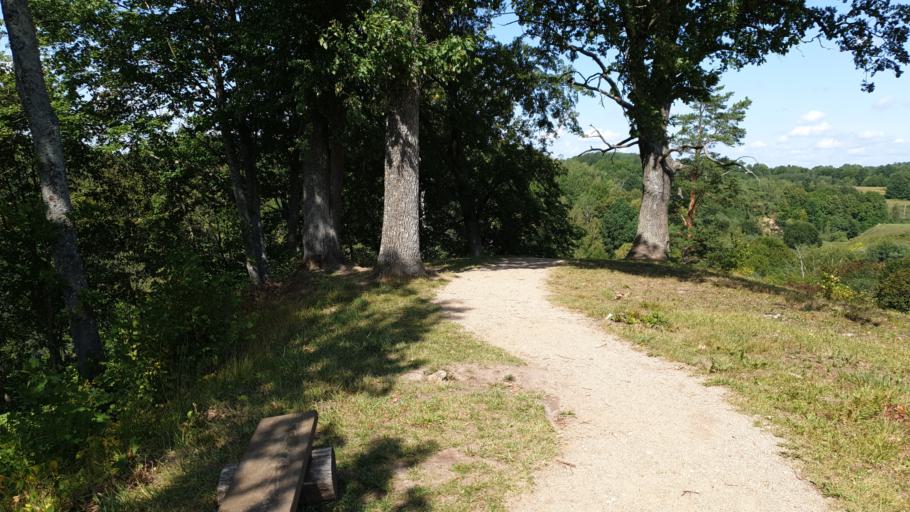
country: LT
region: Vilnius County
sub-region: Vilniaus Rajonas
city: Vievis
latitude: 54.8223
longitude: 24.9405
